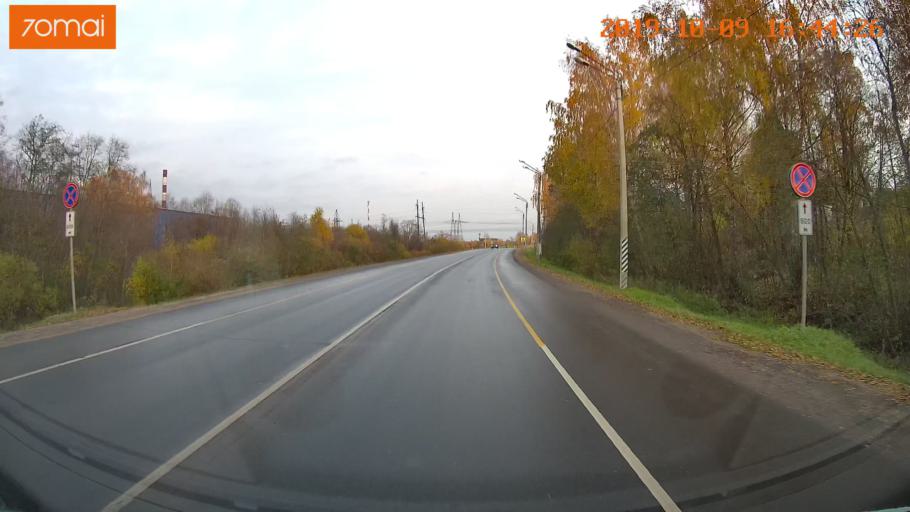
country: RU
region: Kostroma
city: Volgorechensk
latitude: 57.4517
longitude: 41.1408
